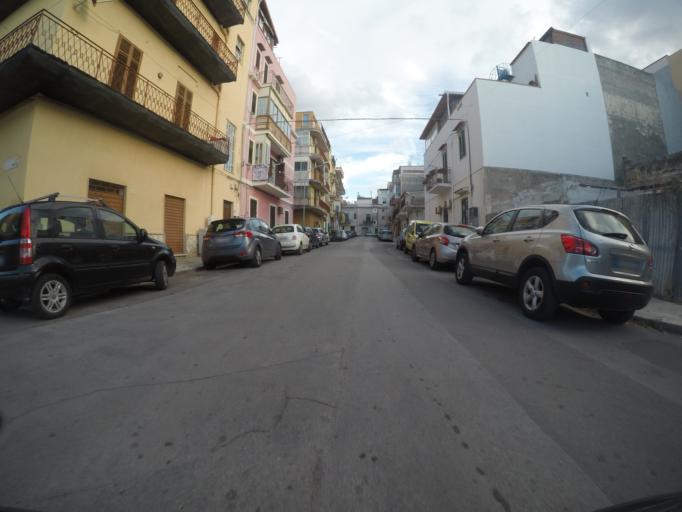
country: IT
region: Sicily
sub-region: Palermo
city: Isola delle Femmine
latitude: 38.2007
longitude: 13.2780
